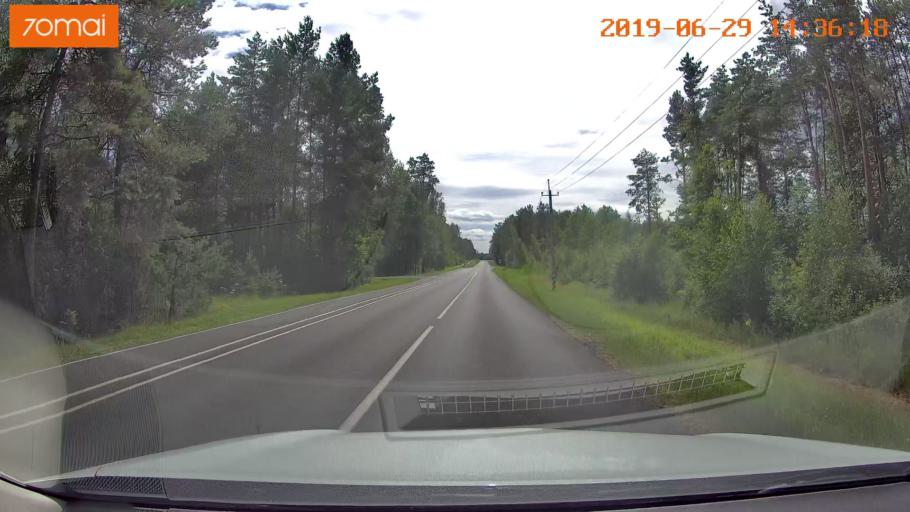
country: BY
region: Minsk
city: Starobin
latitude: 52.7525
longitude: 27.4797
